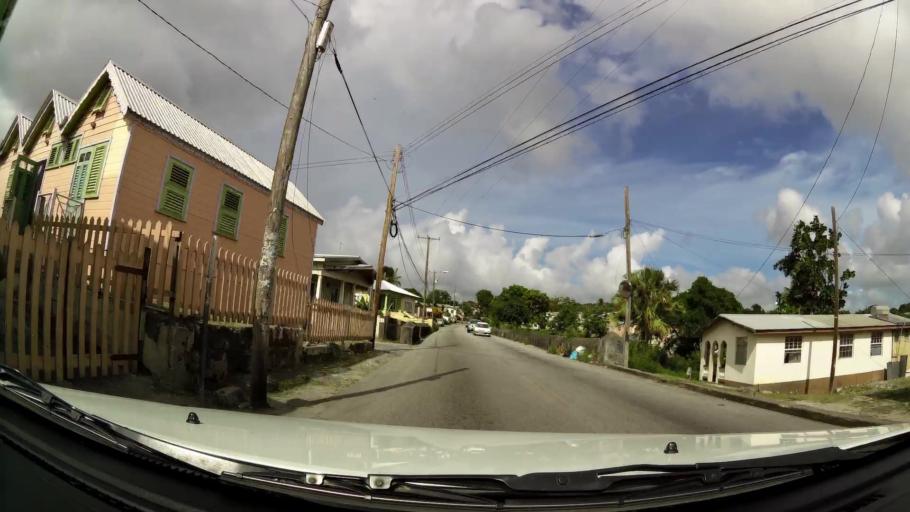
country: BB
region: Saint Michael
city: Bridgetown
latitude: 13.1134
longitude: -59.6026
